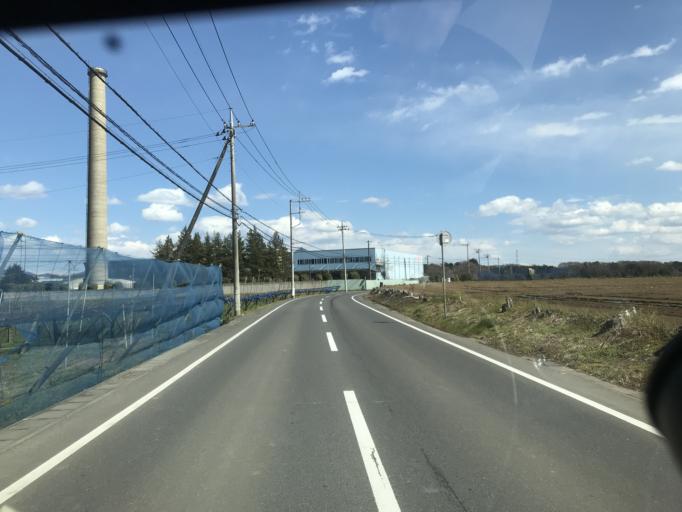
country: JP
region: Ibaraki
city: Shimodate
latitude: 36.2336
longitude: 139.9518
